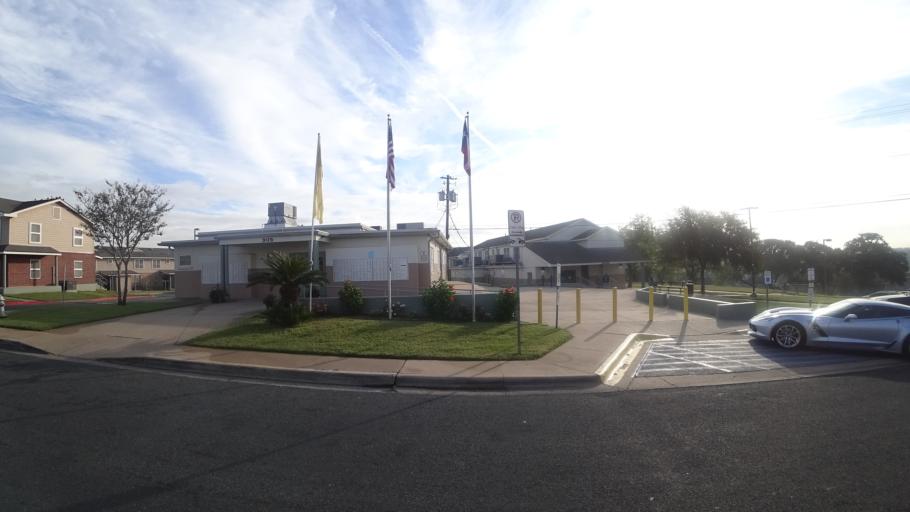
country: US
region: Texas
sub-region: Travis County
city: Austin
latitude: 30.2716
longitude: -97.7078
